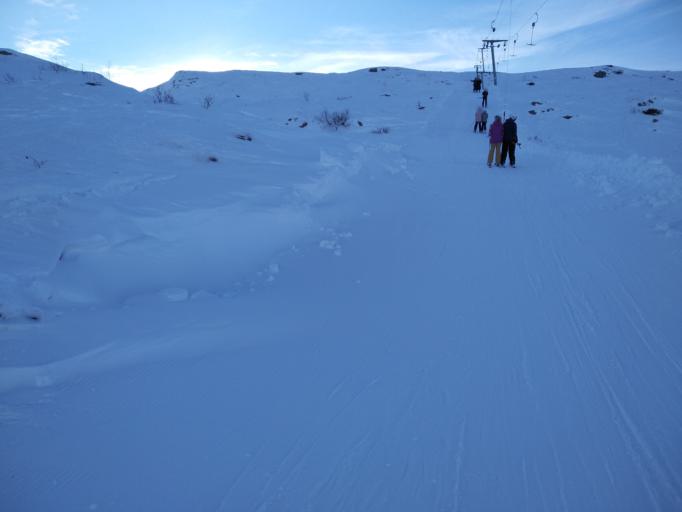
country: NO
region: Rogaland
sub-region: Sauda
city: Sauda
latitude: 59.6161
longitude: 6.2288
